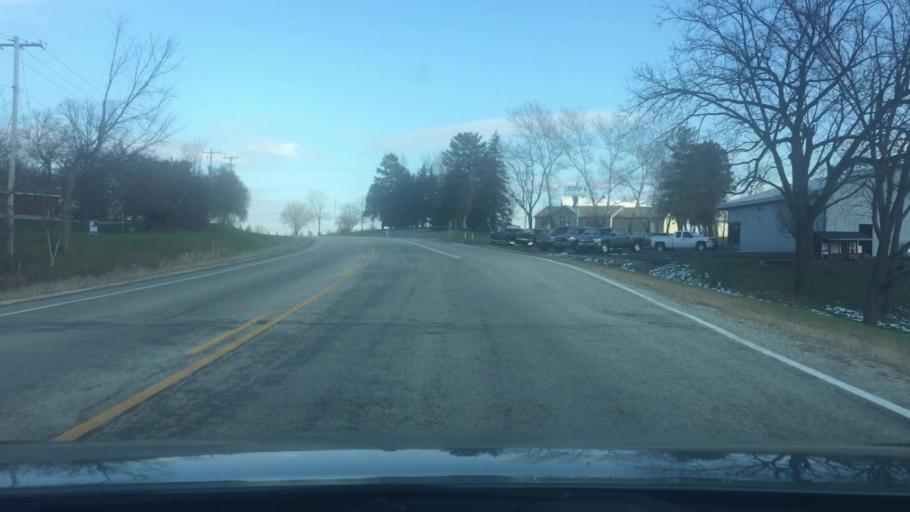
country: US
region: Wisconsin
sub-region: Jefferson County
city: Palmyra
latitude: 42.9309
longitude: -88.6807
